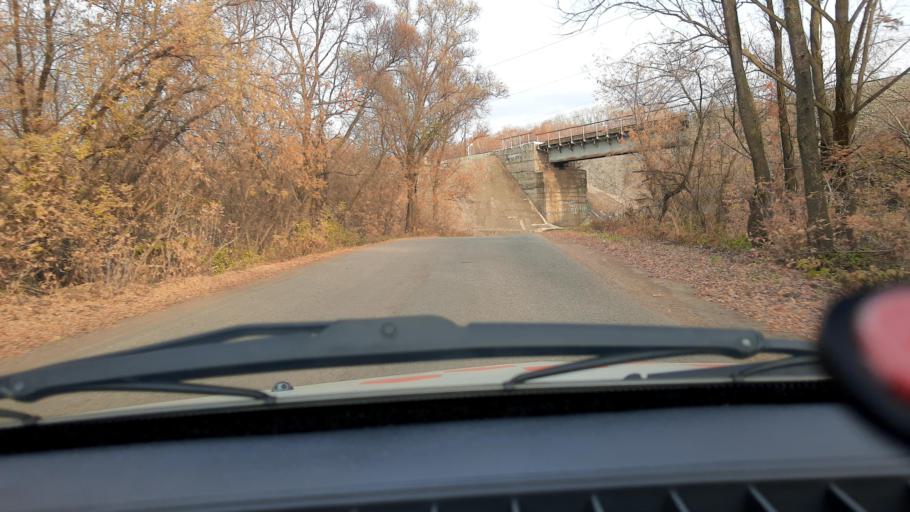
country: RU
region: Bashkortostan
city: Iglino
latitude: 54.7997
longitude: 56.3129
